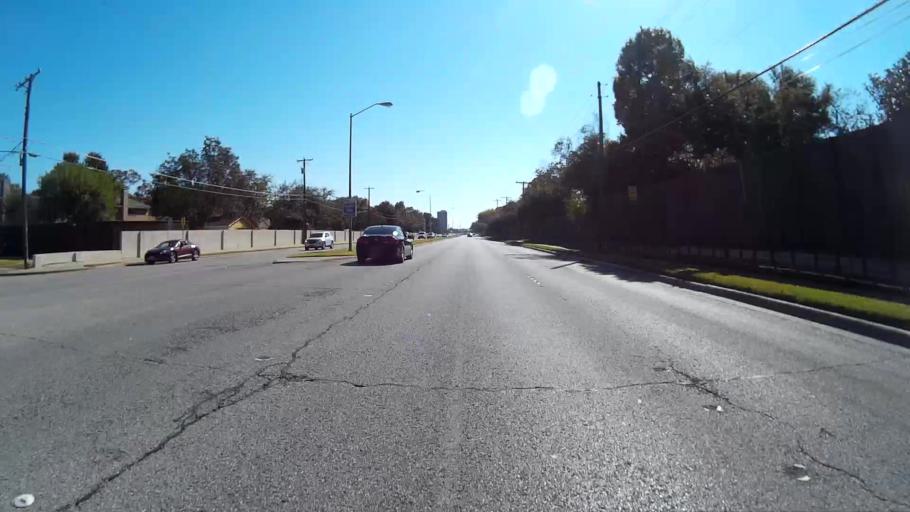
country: US
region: Texas
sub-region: Dallas County
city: Richardson
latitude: 32.9672
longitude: -96.7690
